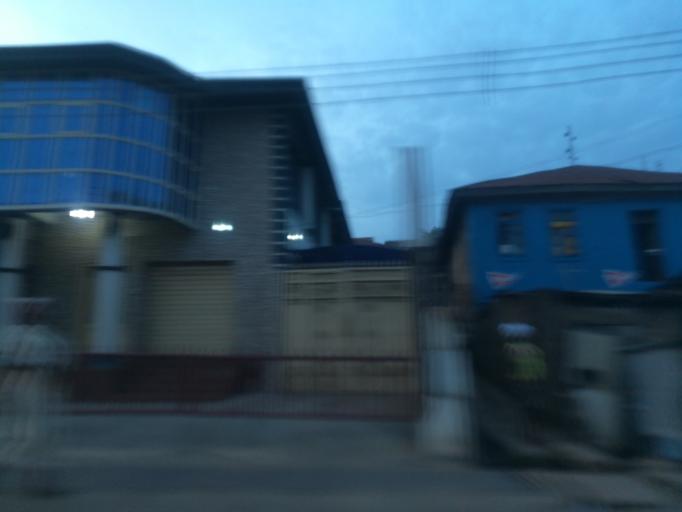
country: NG
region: Oyo
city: Ibadan
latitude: 7.3870
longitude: 3.8996
